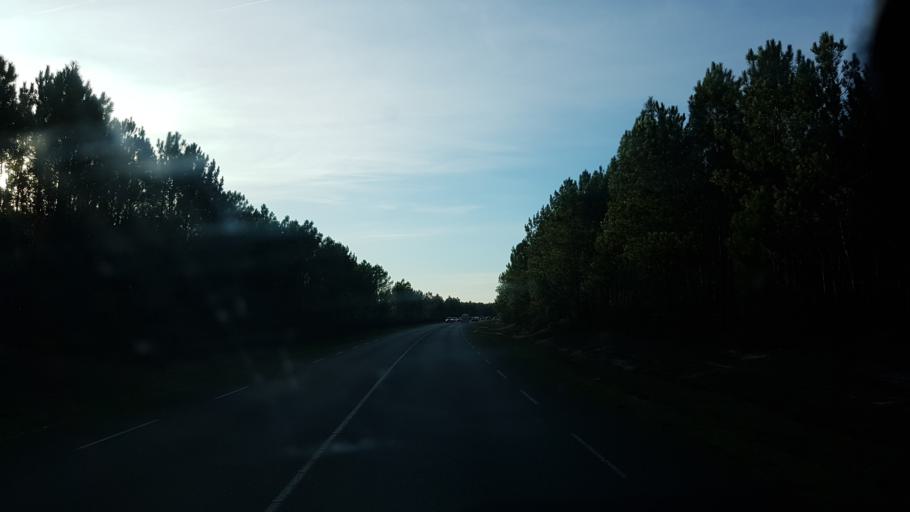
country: FR
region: Aquitaine
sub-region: Departement de la Gironde
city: Martignas-sur-Jalle
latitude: 44.8296
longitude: -0.7829
